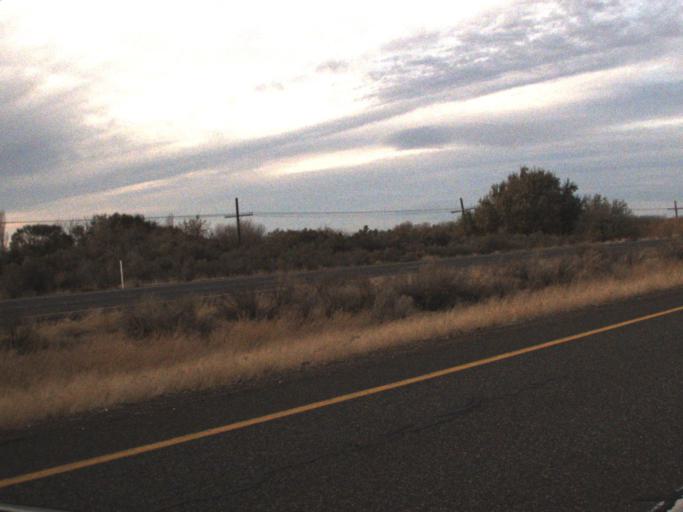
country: US
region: Washington
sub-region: Benton County
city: Finley
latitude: 46.1251
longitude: -118.9305
